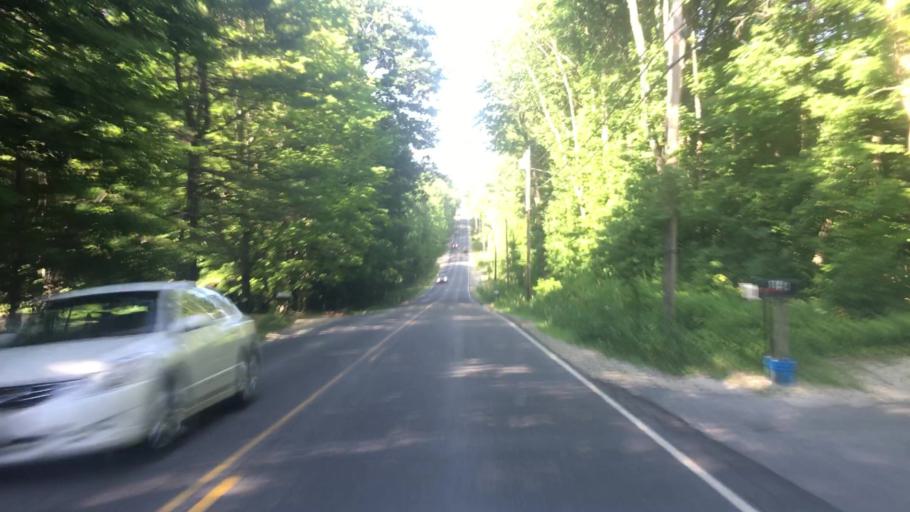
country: US
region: Maine
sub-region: York County
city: Buxton
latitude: 43.7268
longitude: -70.5599
